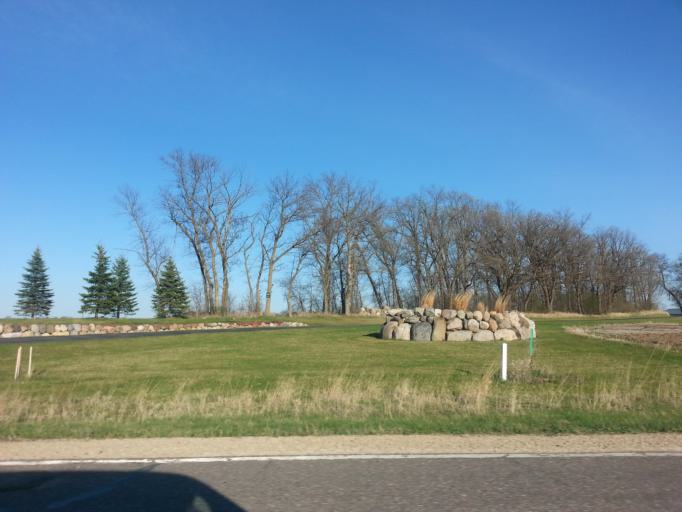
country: US
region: Minnesota
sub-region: Dakota County
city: Lakeville
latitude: 44.5992
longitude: -93.2652
